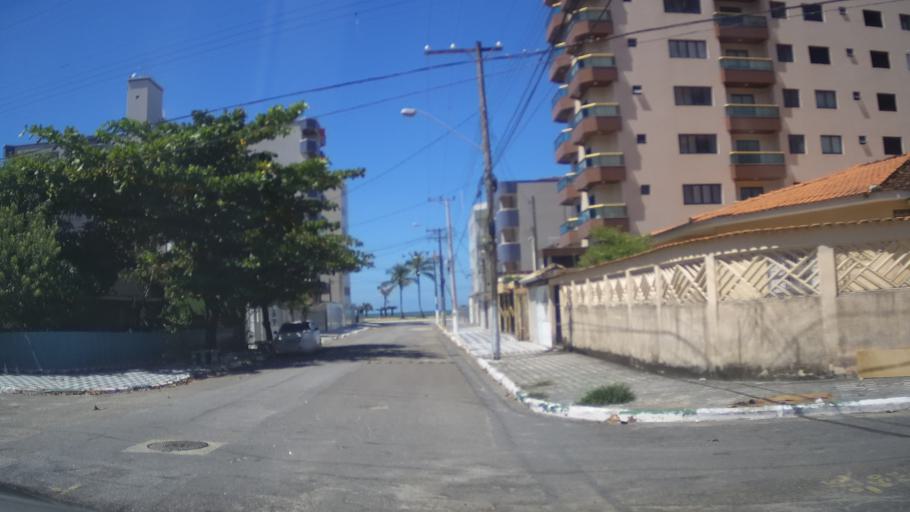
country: BR
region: Sao Paulo
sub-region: Mongagua
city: Mongagua
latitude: -24.0491
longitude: -46.5236
